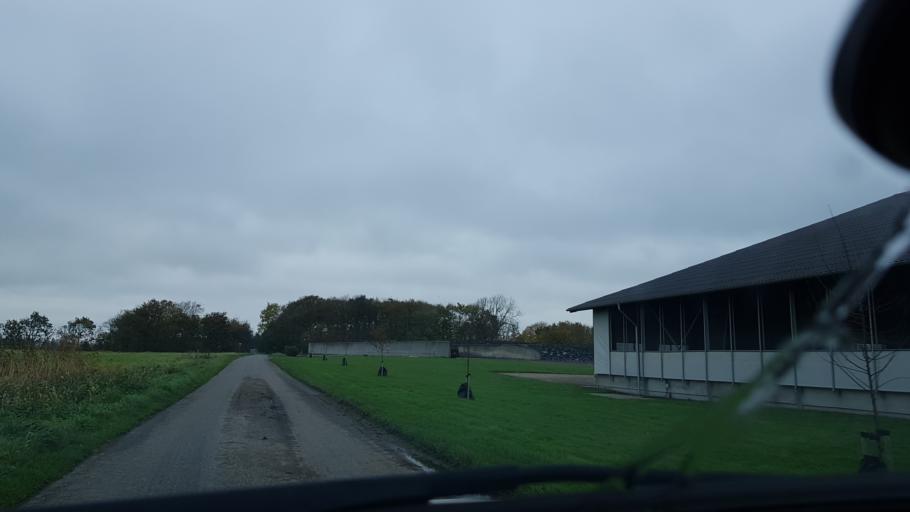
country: DK
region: South Denmark
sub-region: Esbjerg Kommune
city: Ribe
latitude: 55.2632
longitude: 8.8627
